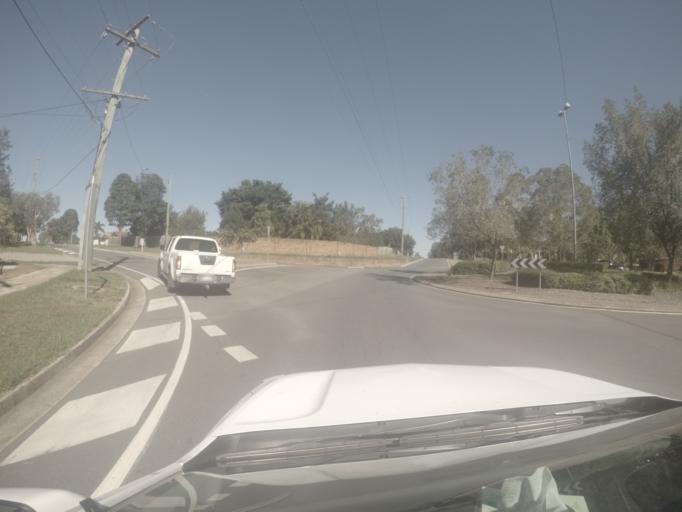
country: AU
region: Queensland
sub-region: Ipswich
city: Springfield
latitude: -27.6437
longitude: 152.9190
